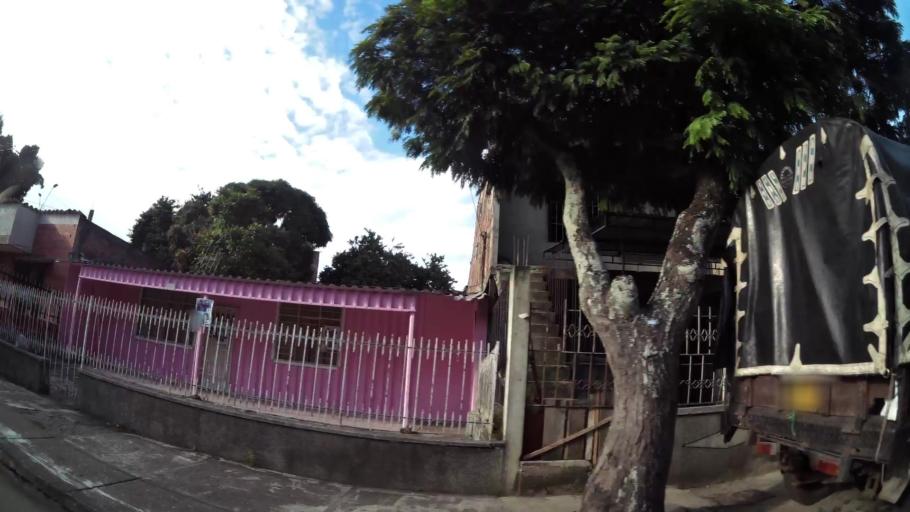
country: CO
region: Valle del Cauca
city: Cali
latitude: 3.4330
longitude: -76.5193
